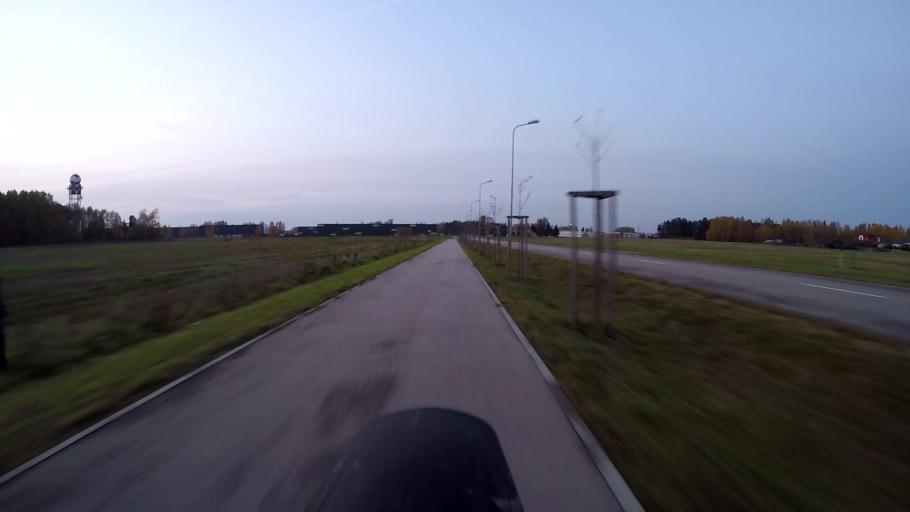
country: LV
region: Marupe
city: Marupe
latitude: 56.9140
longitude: 23.9944
